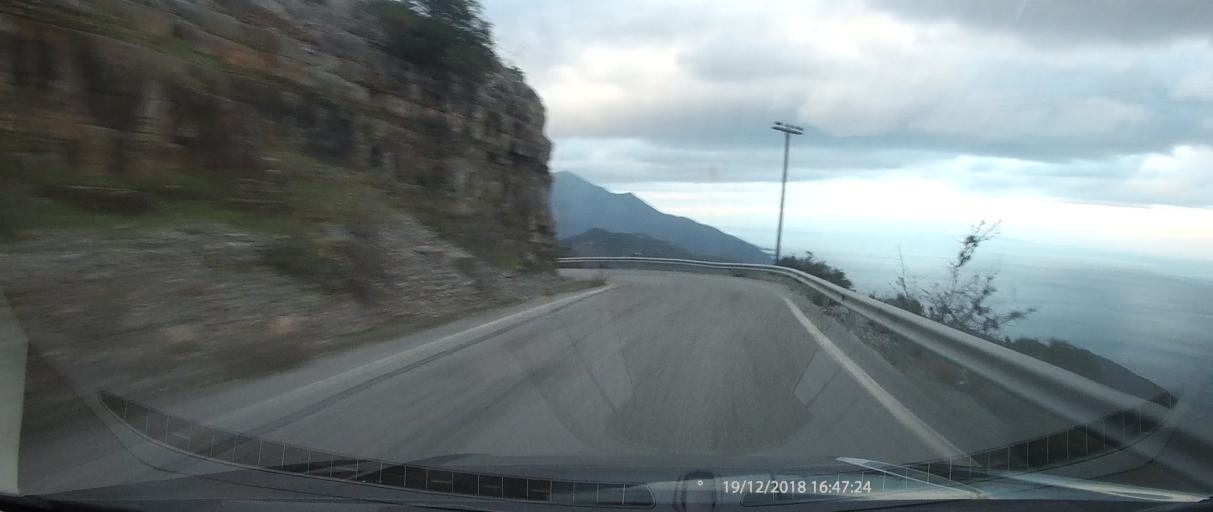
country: GR
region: Peloponnese
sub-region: Nomos Lakonias
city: Sykea
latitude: 36.9288
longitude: 23.0048
